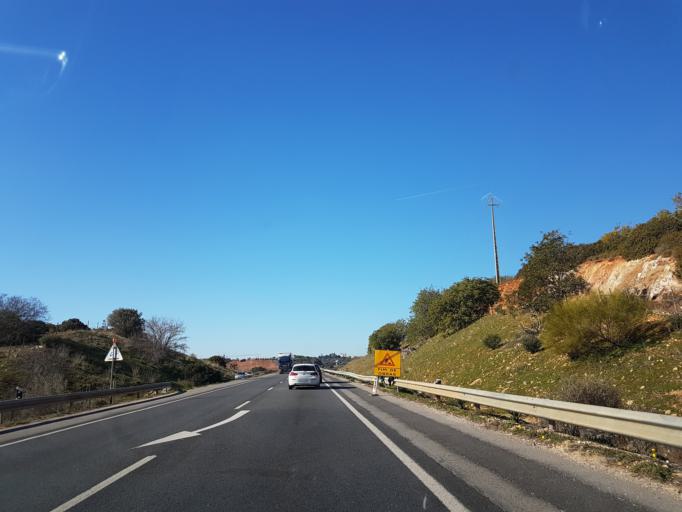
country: PT
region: Faro
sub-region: Portimao
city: Portimao
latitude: 37.1520
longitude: -8.5136
